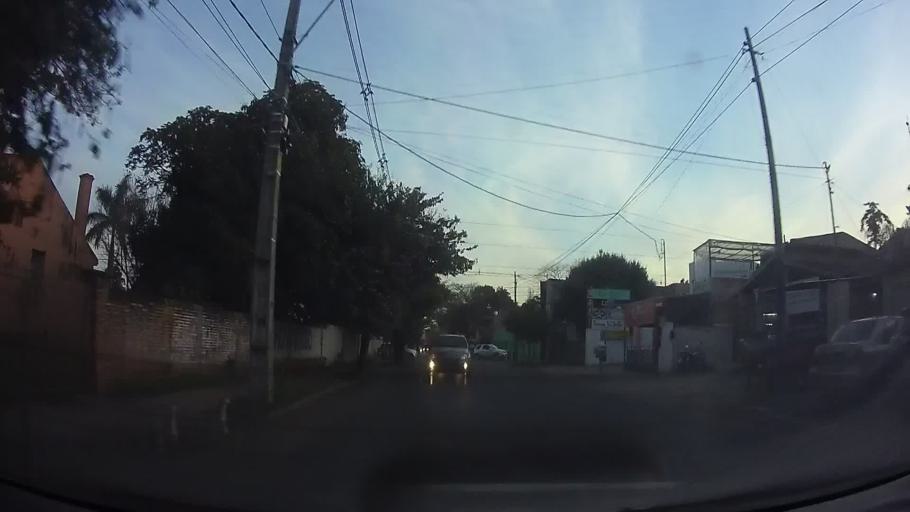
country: PY
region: Central
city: Fernando de la Mora
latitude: -25.2900
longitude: -57.5593
